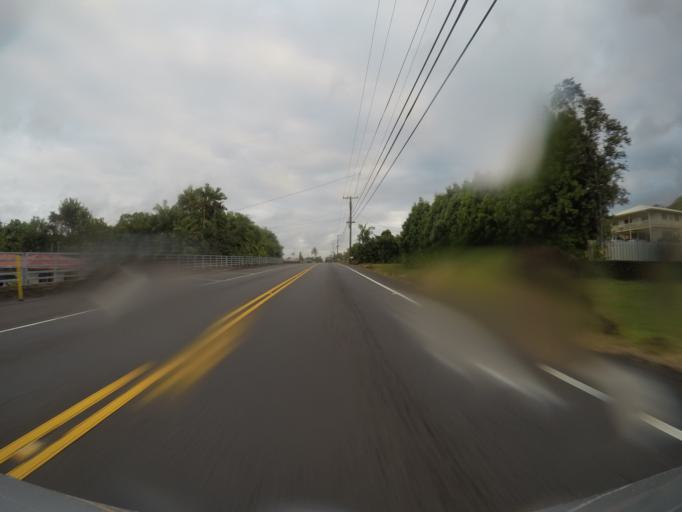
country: US
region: Hawaii
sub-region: Hawaii County
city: Hilo
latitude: 19.6906
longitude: -155.0903
